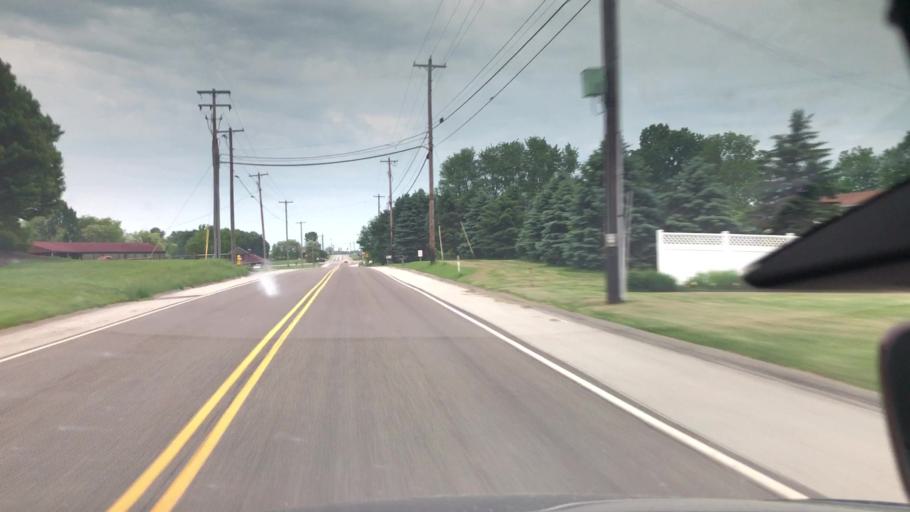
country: US
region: Pennsylvania
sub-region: Butler County
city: Saxonburg
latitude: 40.7256
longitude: -79.8529
